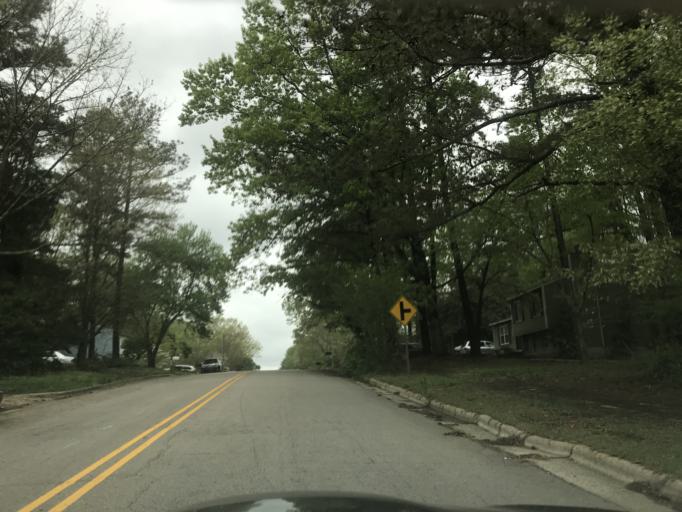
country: US
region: North Carolina
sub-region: Wake County
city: West Raleigh
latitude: 35.7517
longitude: -78.6758
